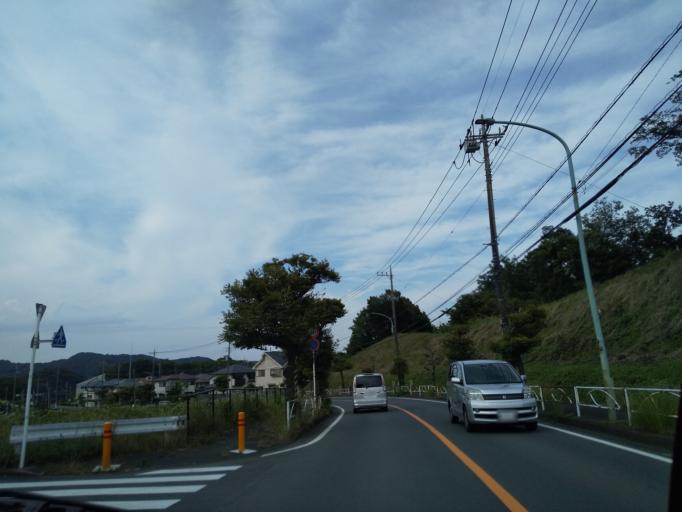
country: JP
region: Kanagawa
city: Atsugi
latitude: 35.4775
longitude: 139.3166
